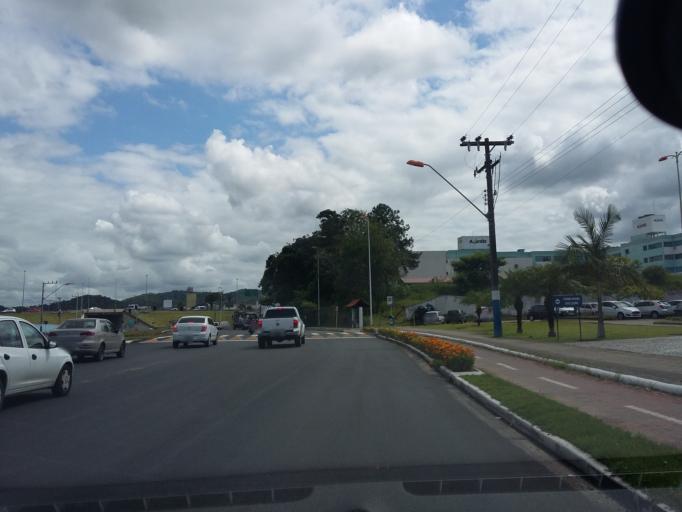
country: BR
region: Santa Catarina
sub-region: Balneario Camboriu
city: Balneario Camboriu
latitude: -26.9953
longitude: -48.6530
